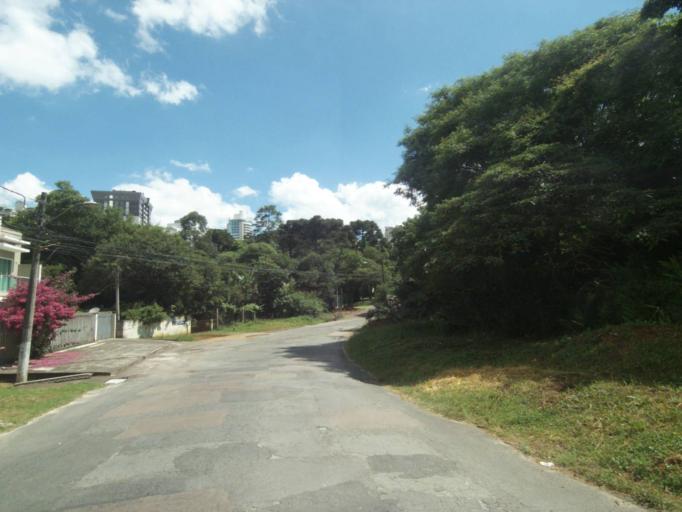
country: BR
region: Parana
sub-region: Curitiba
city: Curitiba
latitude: -25.4342
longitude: -49.3310
